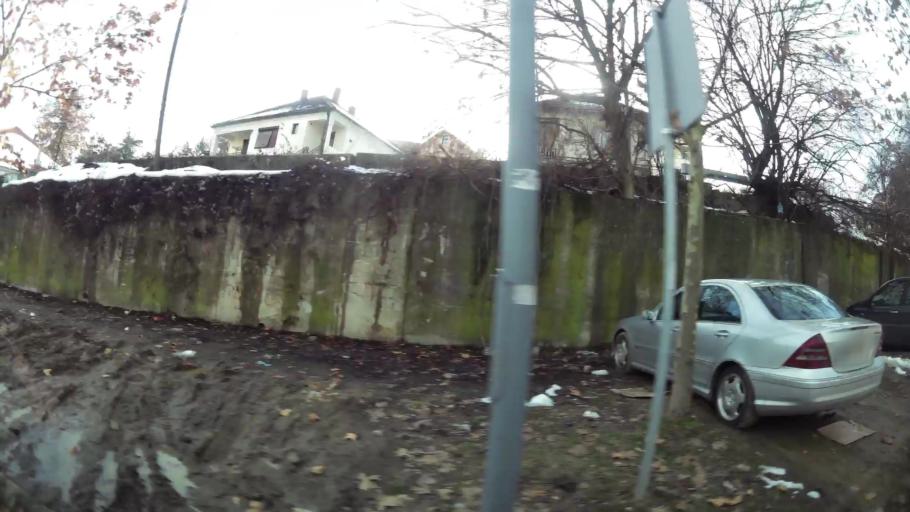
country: RS
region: Central Serbia
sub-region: Belgrade
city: Rakovica
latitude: 44.7333
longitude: 20.4266
